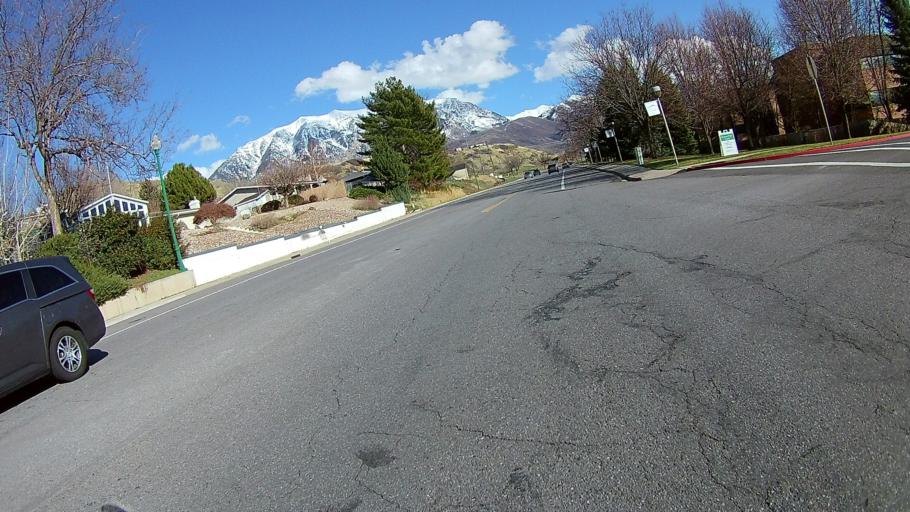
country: US
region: Utah
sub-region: Utah County
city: Orem
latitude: 40.3258
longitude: -111.6784
